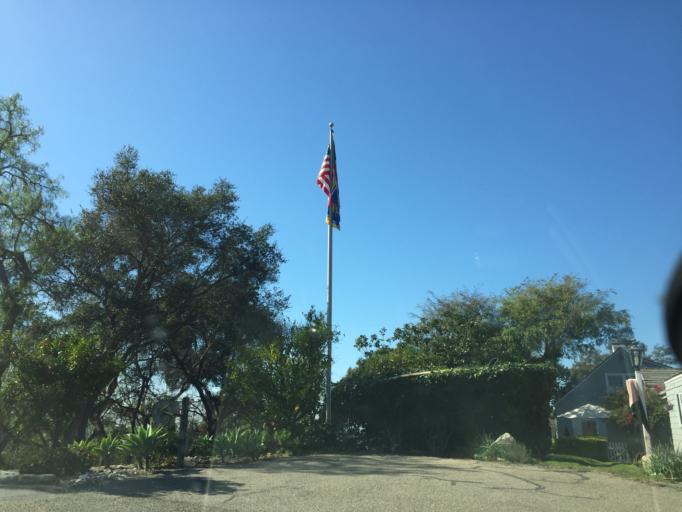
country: US
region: California
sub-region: Santa Barbara County
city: Mission Canyon
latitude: 34.4354
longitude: -119.7649
